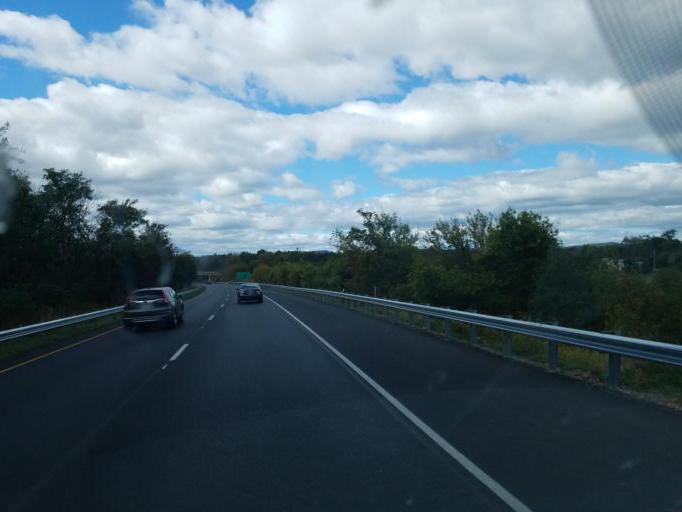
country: US
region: Maryland
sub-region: Washington County
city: Wilson-Conococheague
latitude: 39.6504
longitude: -77.8488
